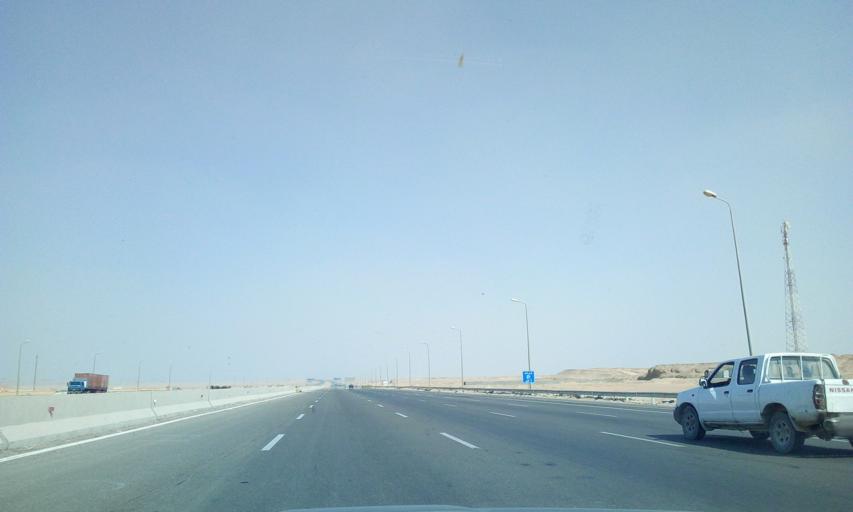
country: EG
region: Muhafazat al Qahirah
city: Halwan
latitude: 29.9044
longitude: 31.7492
